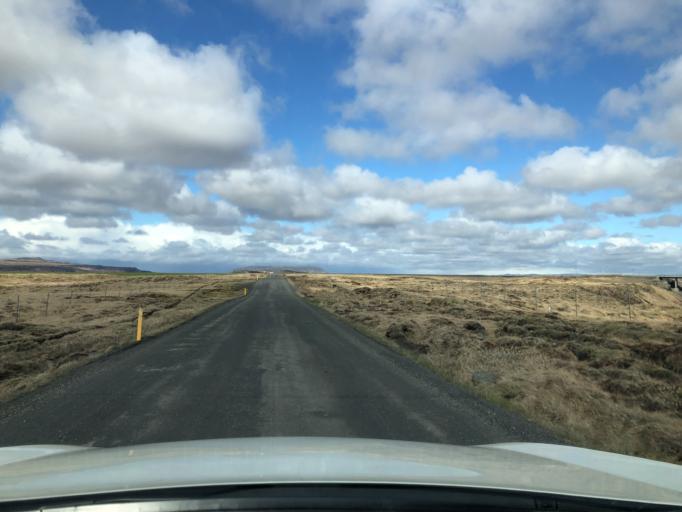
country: IS
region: South
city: Selfoss
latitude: 63.9282
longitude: -20.6724
